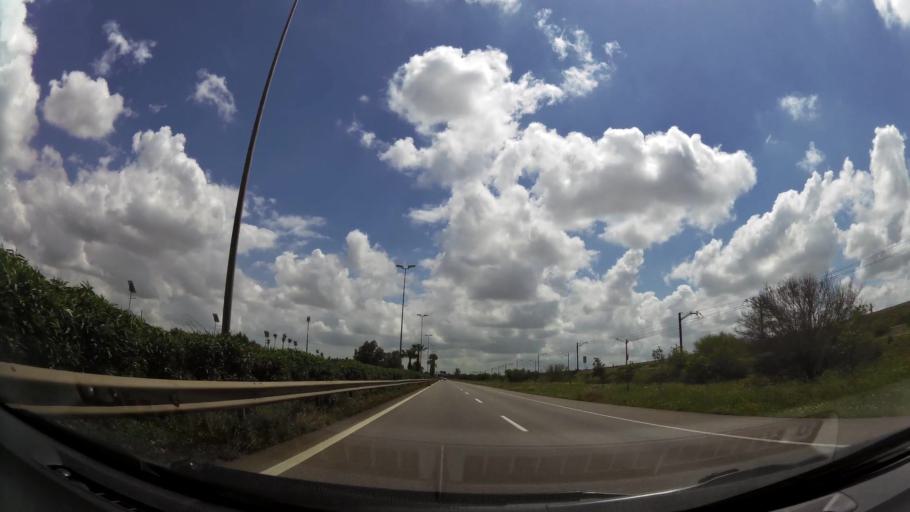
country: MA
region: Chaouia-Ouardigha
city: Nouaseur
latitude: 33.4080
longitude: -7.6252
